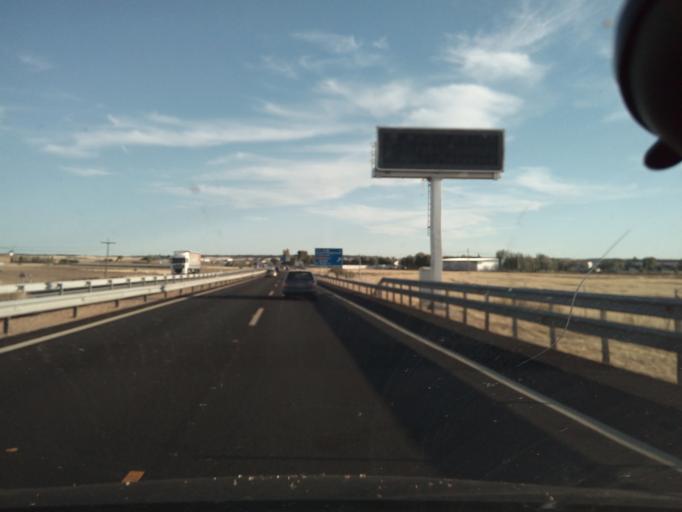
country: ES
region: Castille-La Mancha
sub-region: Province of Toledo
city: Tembleque
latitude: 39.7067
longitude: -3.4972
